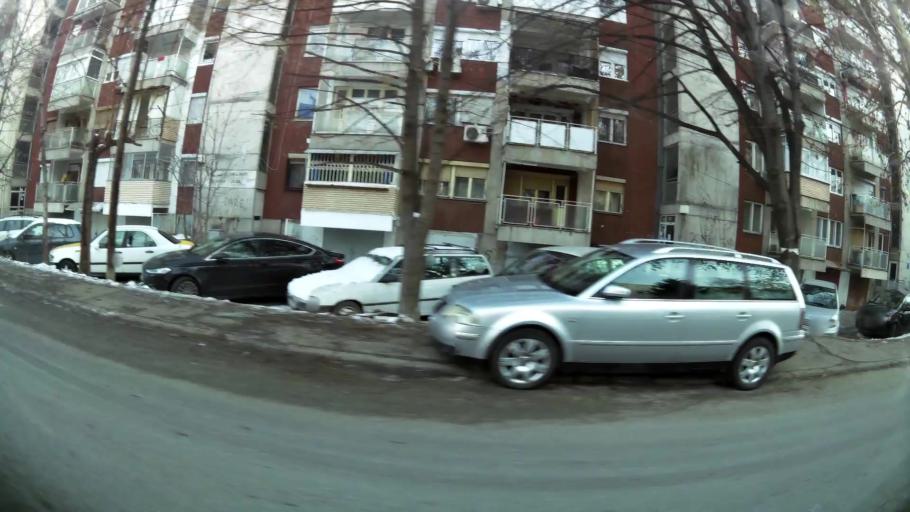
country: MK
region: Cair
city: Cair
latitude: 42.0208
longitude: 21.4323
